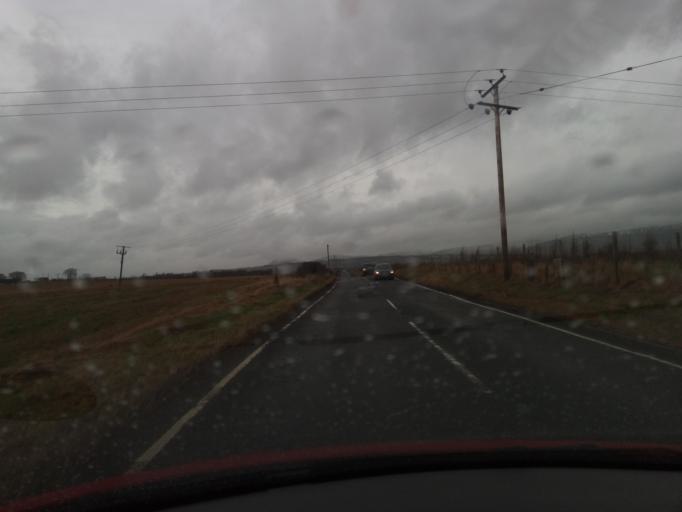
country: GB
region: Scotland
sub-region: East Dunbartonshire
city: Bishopbriggs
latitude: 55.9198
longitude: -4.1853
